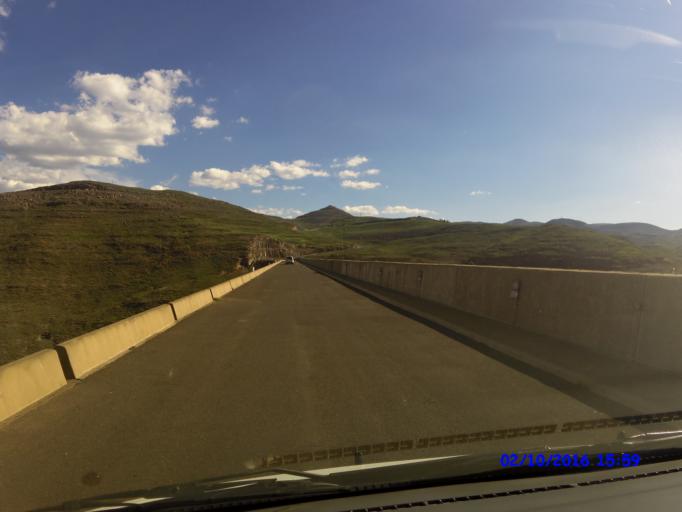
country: LS
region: Maseru
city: Nako
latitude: -29.4569
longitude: 28.0969
